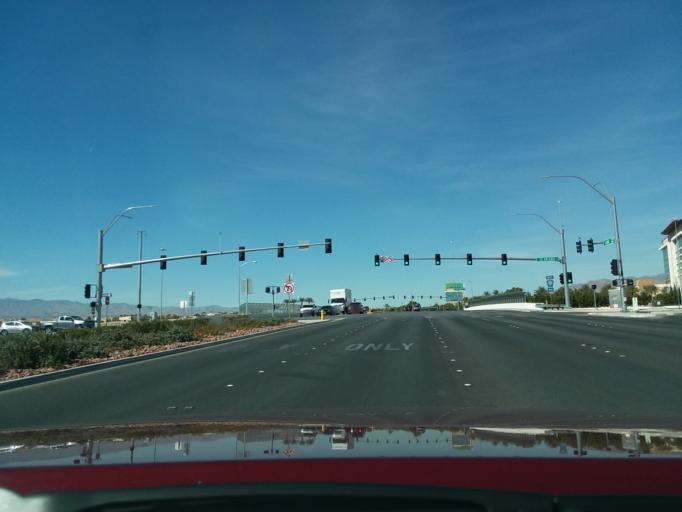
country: US
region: Nevada
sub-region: Clark County
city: North Las Vegas
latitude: 36.2890
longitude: -115.1791
